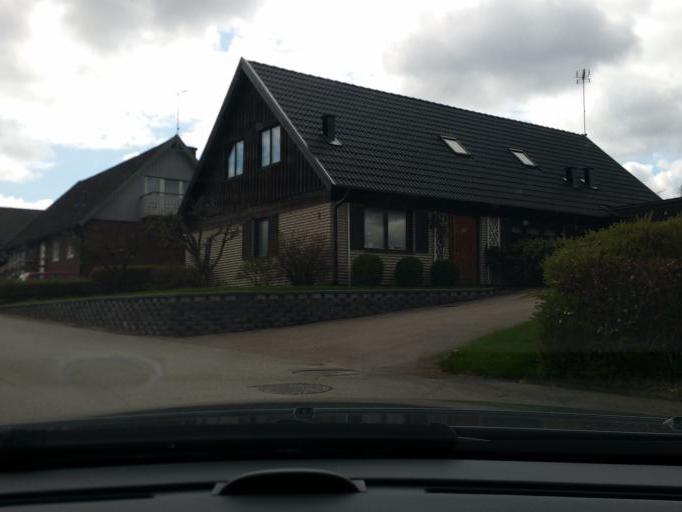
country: SE
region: Kronoberg
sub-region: Vaxjo Kommun
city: Lammhult
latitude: 57.1716
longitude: 14.5772
